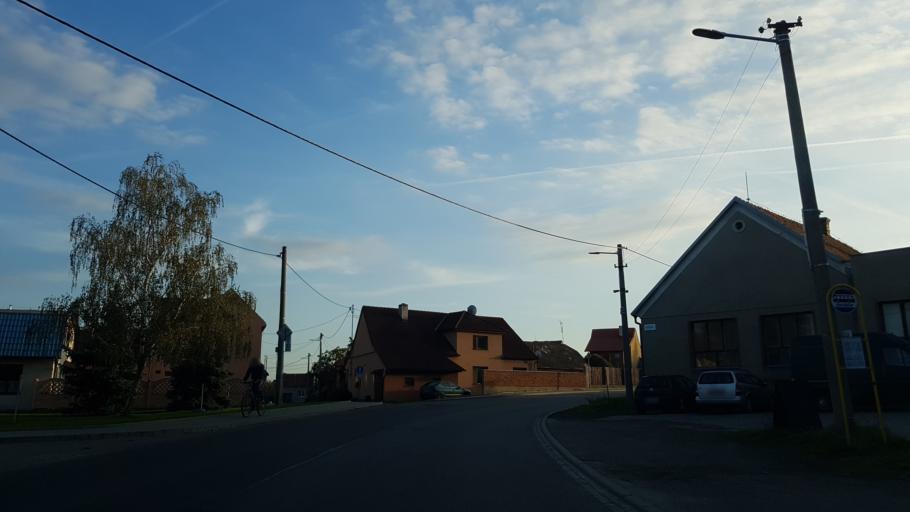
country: CZ
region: Zlin
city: Nedakonice
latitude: 49.0331
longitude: 17.3818
